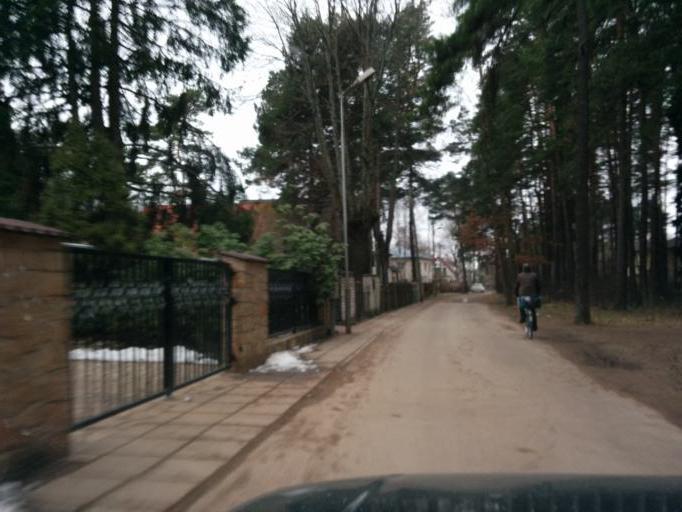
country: LV
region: Jurmala
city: Jurmala
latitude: 56.9676
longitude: 23.8385
